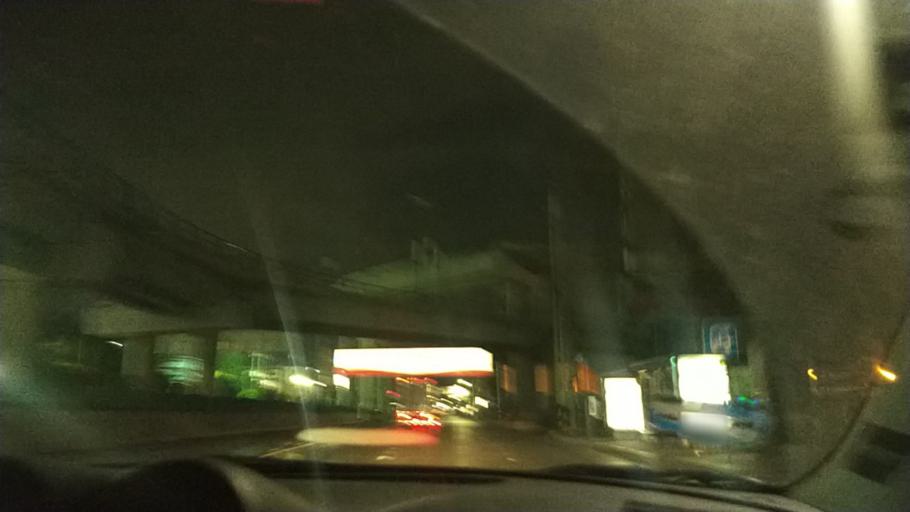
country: MX
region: Mexico
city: Ecatepec
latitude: 19.6262
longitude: -99.0791
